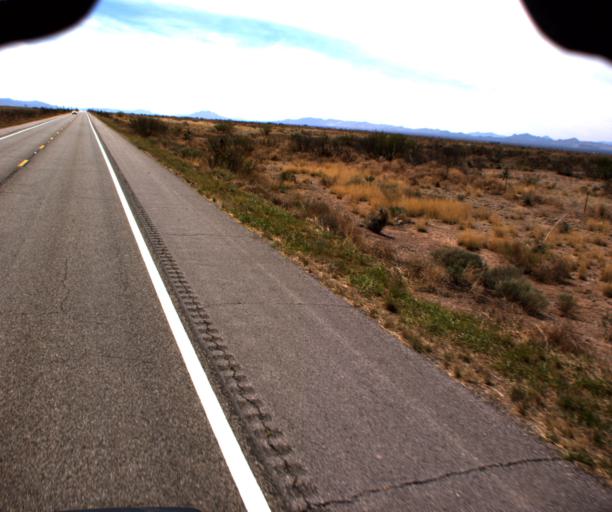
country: US
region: Arizona
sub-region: Cochise County
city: Pirtleville
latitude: 31.5485
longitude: -109.6611
